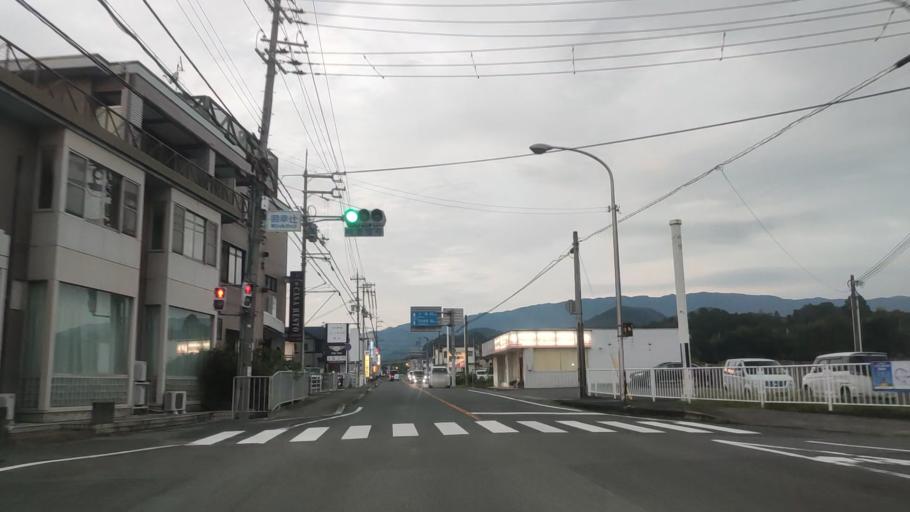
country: JP
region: Wakayama
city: Hashimoto
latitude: 34.3382
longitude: 135.6057
